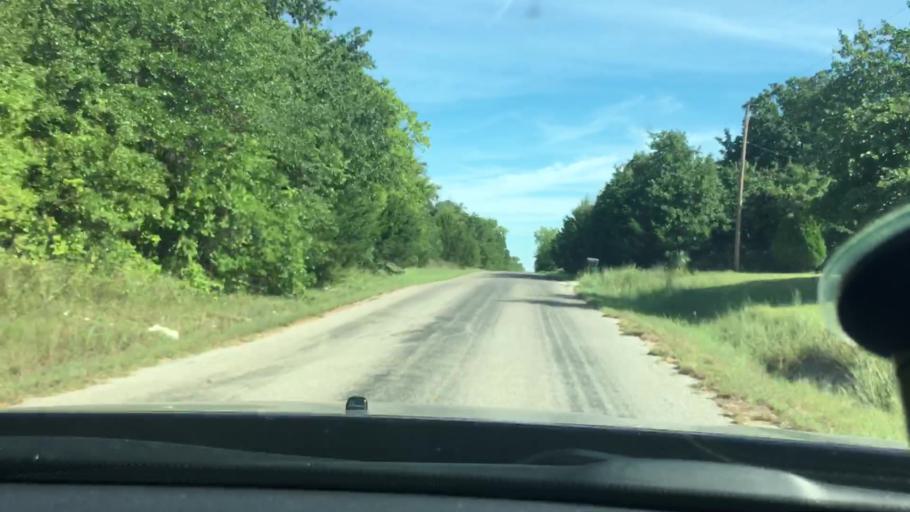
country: US
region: Oklahoma
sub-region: Carter County
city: Lone Grove
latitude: 34.2495
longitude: -97.2475
